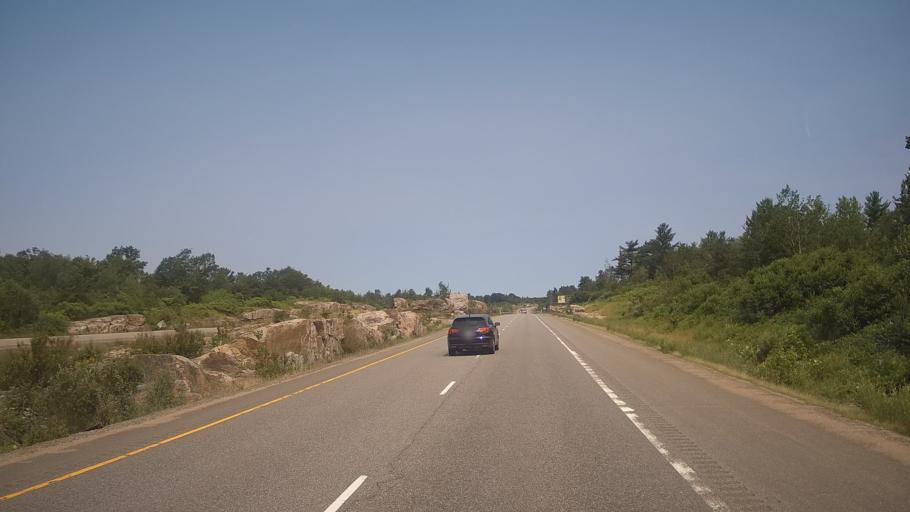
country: CA
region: Ontario
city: Midland
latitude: 44.8634
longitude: -79.7438
